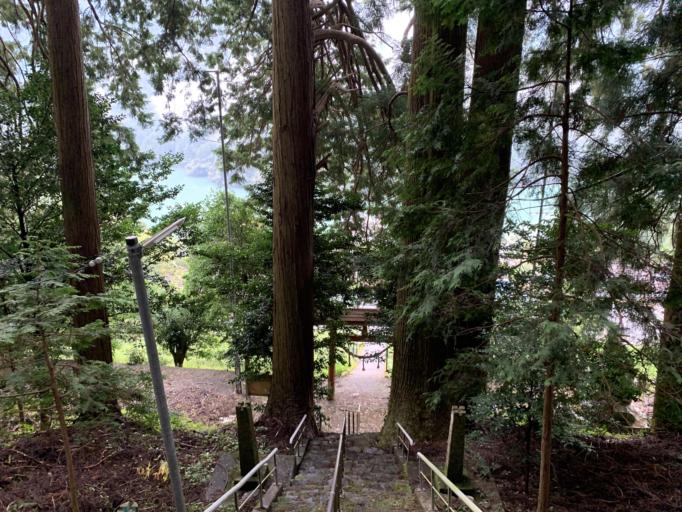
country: JP
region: Nagano
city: Iida
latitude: 35.1914
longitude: 137.8072
